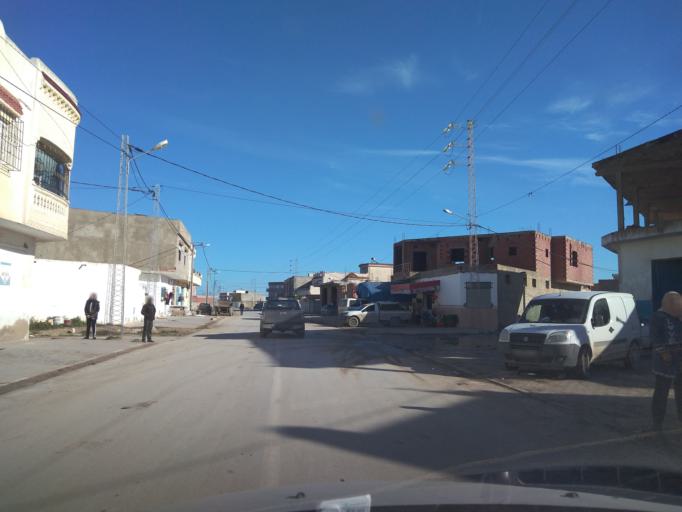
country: TN
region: Ariana
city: Qal'at al Andalus
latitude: 37.0606
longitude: 10.1265
